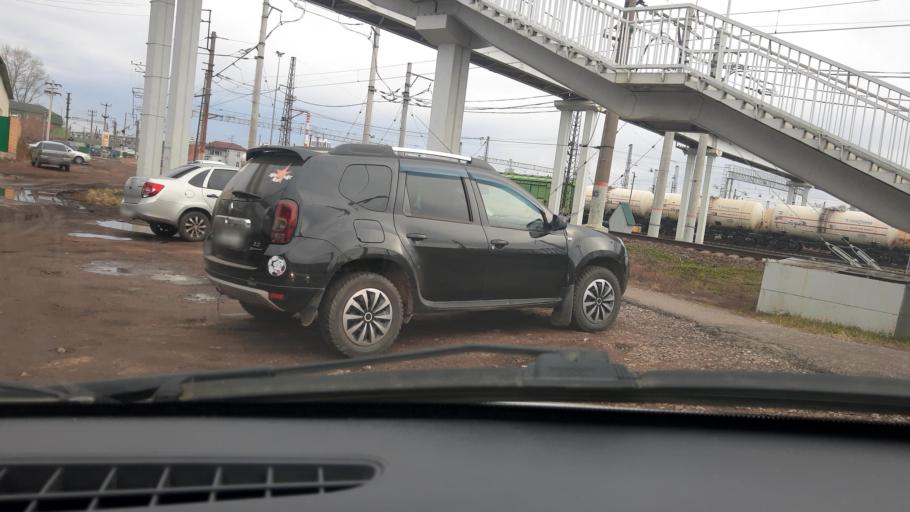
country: RU
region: Bashkortostan
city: Mikhaylovka
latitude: 54.6979
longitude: 55.8354
